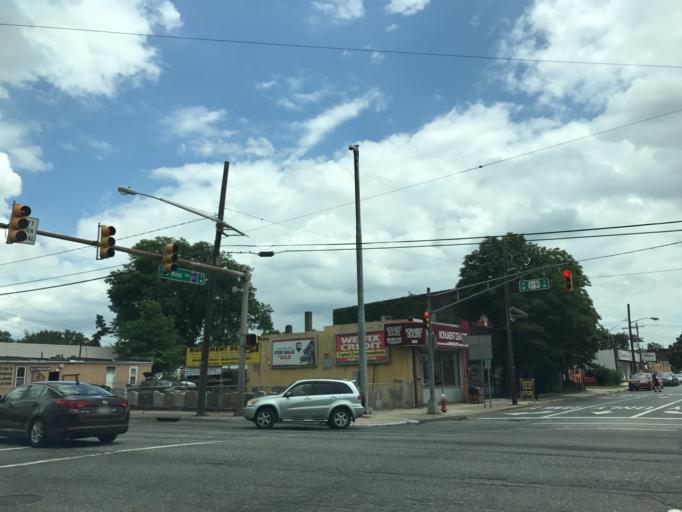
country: US
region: New Jersey
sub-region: Union County
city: Linden
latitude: 40.6266
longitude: -74.2434
